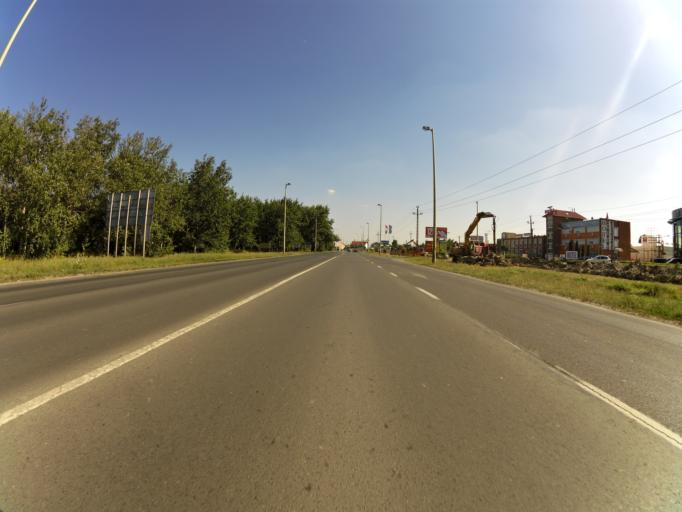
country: HU
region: Csongrad
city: Szeged
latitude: 46.2706
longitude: 20.1027
